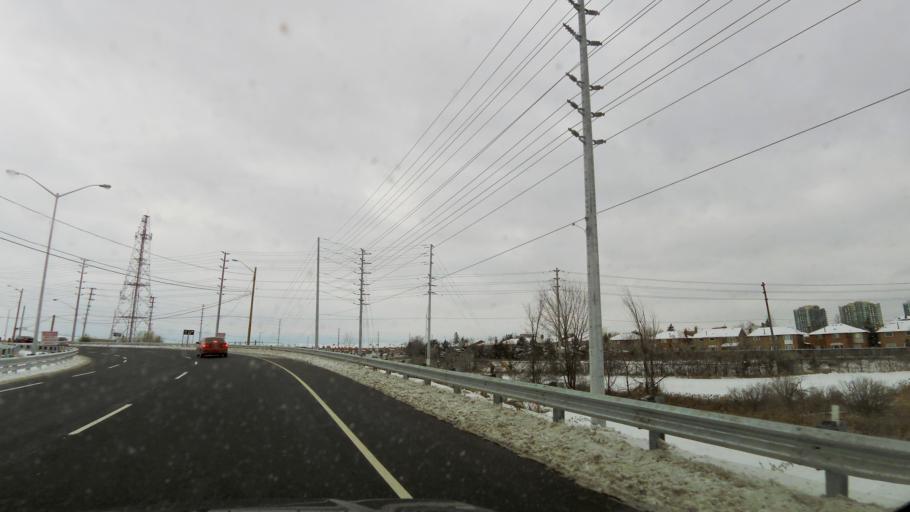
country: CA
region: Ontario
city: Mississauga
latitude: 43.5452
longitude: -79.7092
